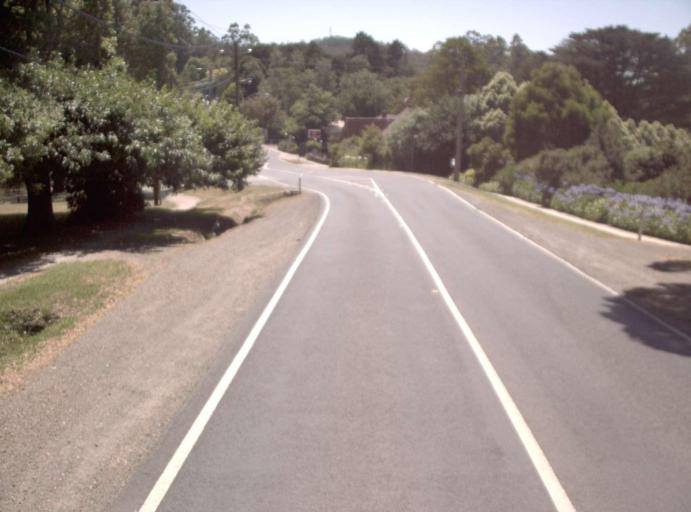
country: AU
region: Victoria
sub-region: Yarra Ranges
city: Olinda
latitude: -37.8492
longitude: 145.3619
